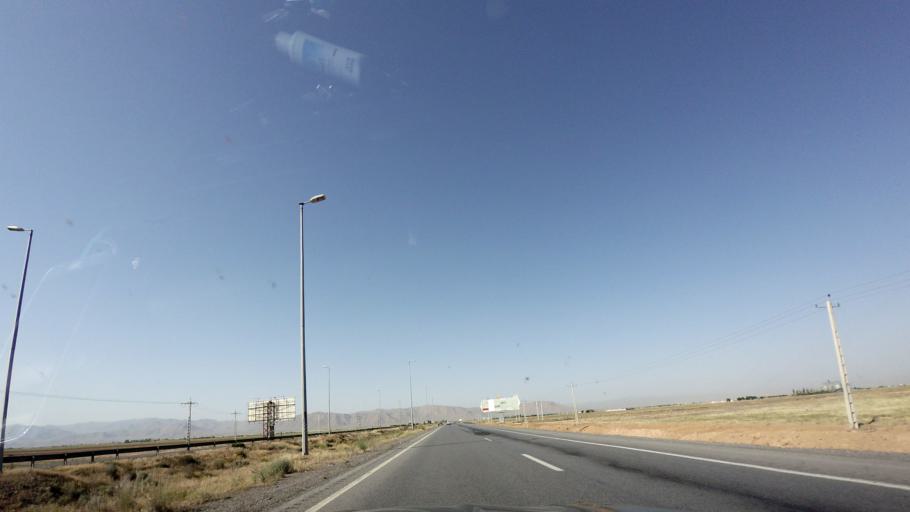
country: IR
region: Markazi
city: Ashtian
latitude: 34.1959
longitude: 50.0578
